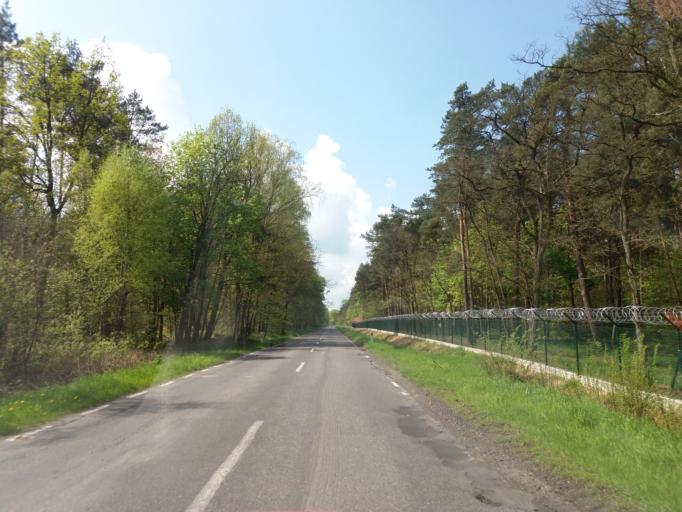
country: PL
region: West Pomeranian Voivodeship
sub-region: Powiat choszczenski
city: Drawno
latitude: 53.2318
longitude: 15.8012
